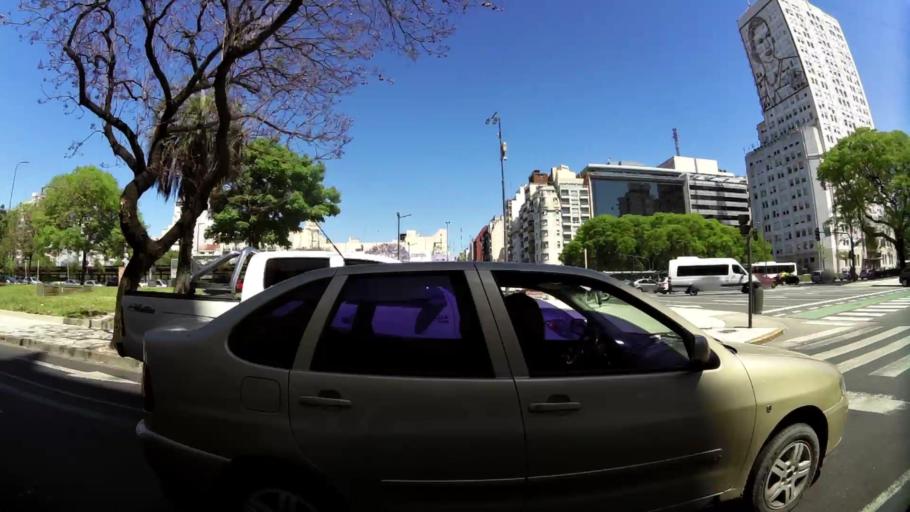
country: AR
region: Buenos Aires F.D.
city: Buenos Aires
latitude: -34.6132
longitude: -58.3805
